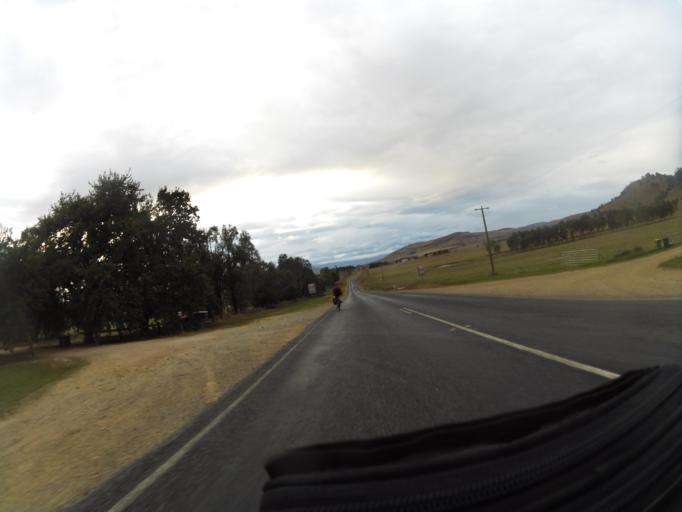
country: AU
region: New South Wales
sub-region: Greater Hume Shire
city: Holbrook
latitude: -36.0528
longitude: 147.9357
